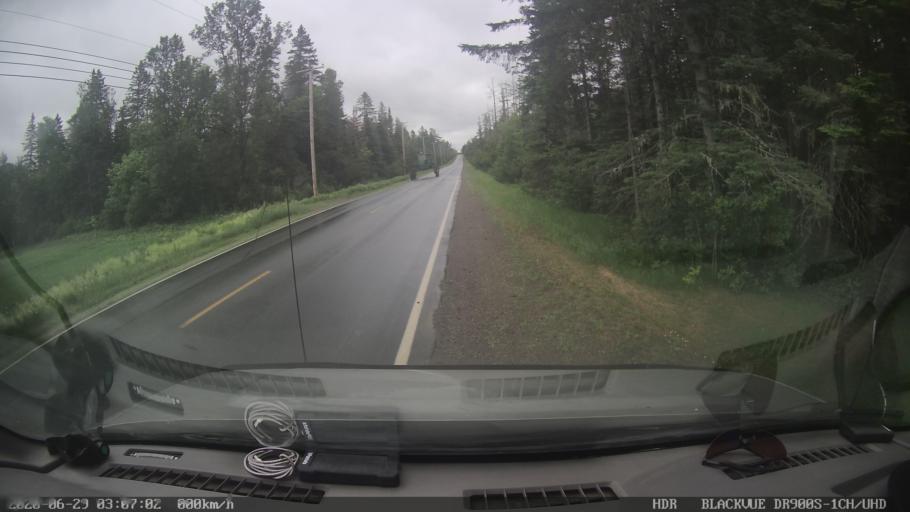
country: US
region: Maine
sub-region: Penobscot County
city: Patten
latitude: 45.8758
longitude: -68.4740
